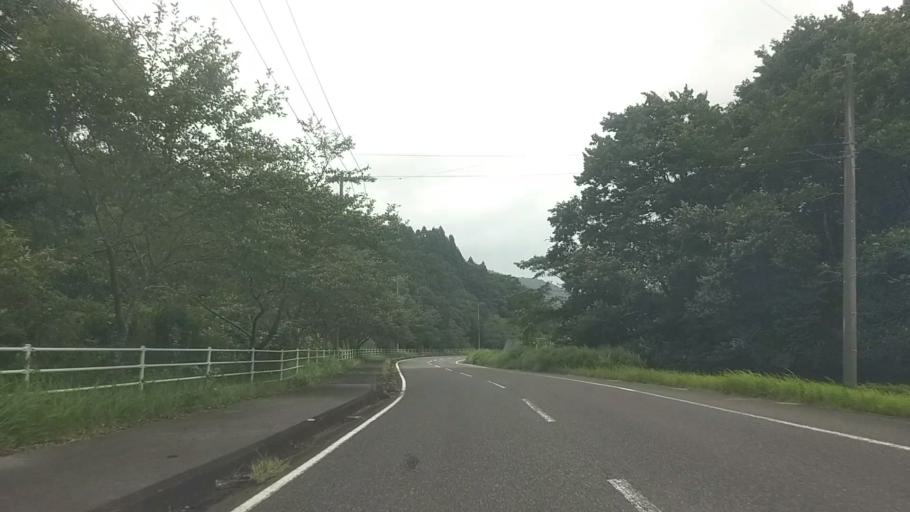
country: JP
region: Chiba
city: Kawaguchi
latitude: 35.2458
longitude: 140.0381
